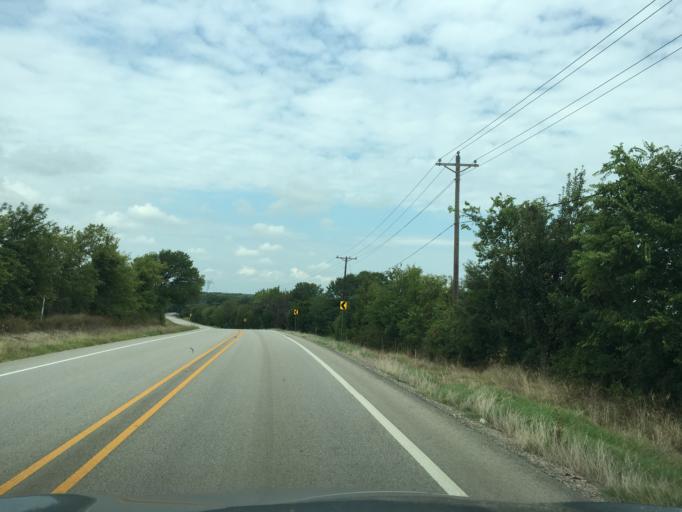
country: US
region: Texas
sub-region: Collin County
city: Anna
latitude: 33.3455
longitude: -96.6028
